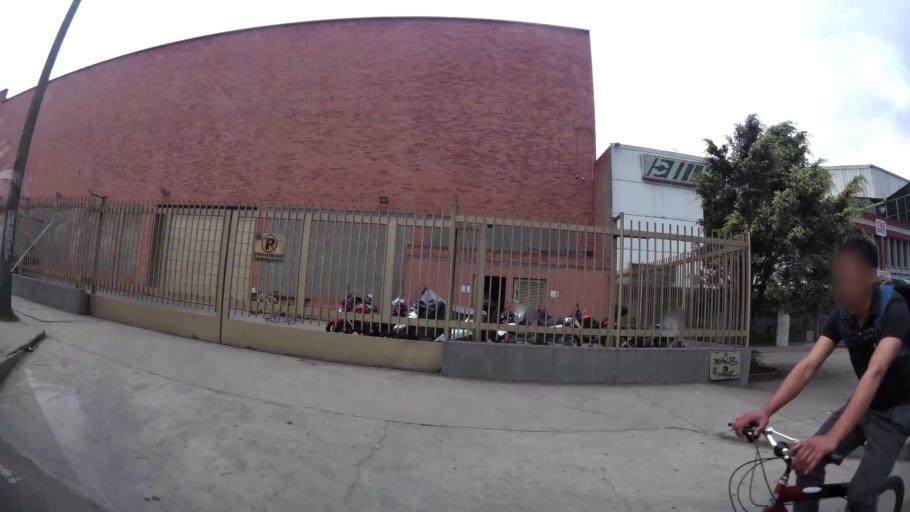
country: CO
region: Bogota D.C.
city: Bogota
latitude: 4.6334
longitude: -74.1207
